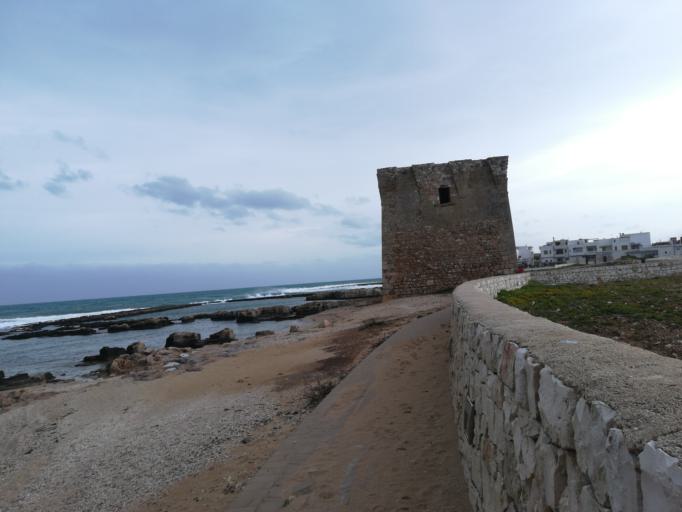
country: IT
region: Apulia
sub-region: Provincia di Bari
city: Polignano a Mare
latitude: 41.0151
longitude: 17.1922
